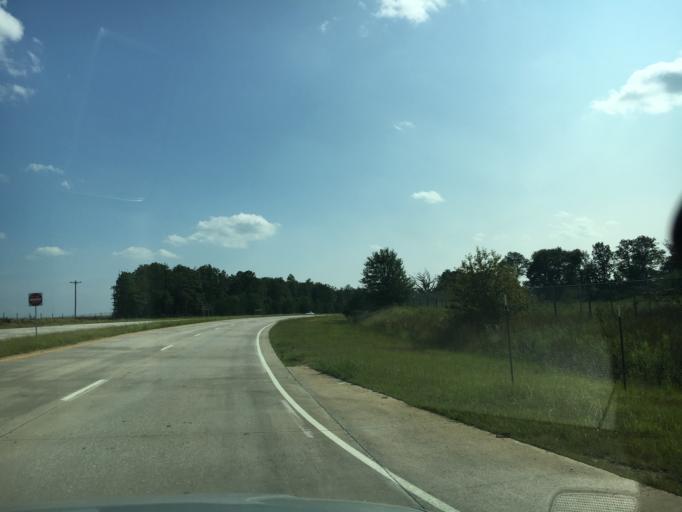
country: US
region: South Carolina
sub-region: Greenville County
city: Greer
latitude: 34.9031
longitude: -82.2194
